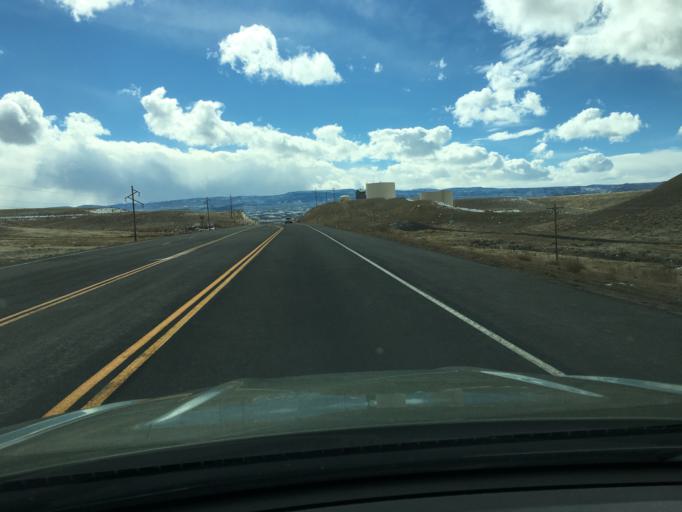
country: US
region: Colorado
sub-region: Mesa County
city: Fruitvale
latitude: 39.0193
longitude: -108.4693
